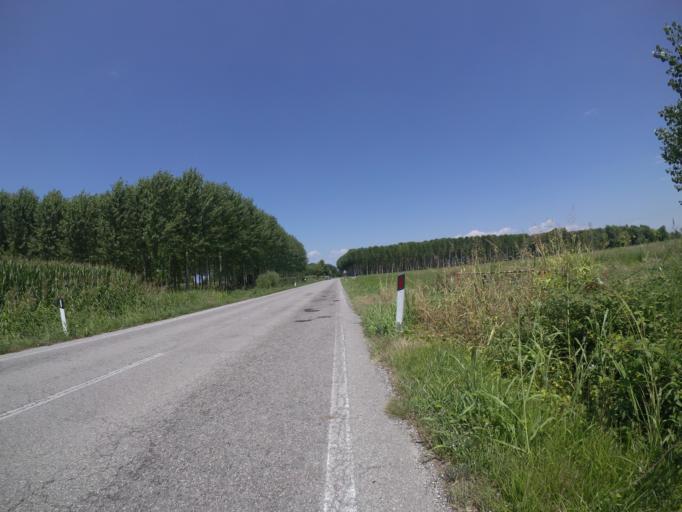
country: IT
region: Friuli Venezia Giulia
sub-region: Provincia di Udine
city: Talmassons
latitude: 45.9091
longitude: 13.1366
